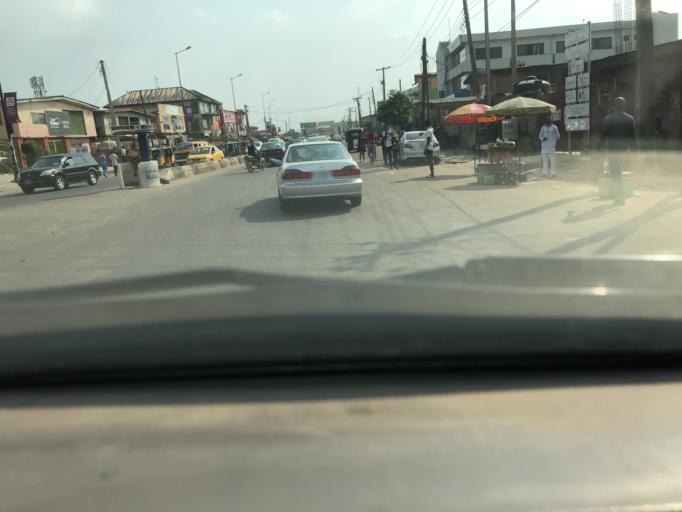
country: NG
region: Lagos
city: Agege
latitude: 6.6056
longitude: 3.3099
